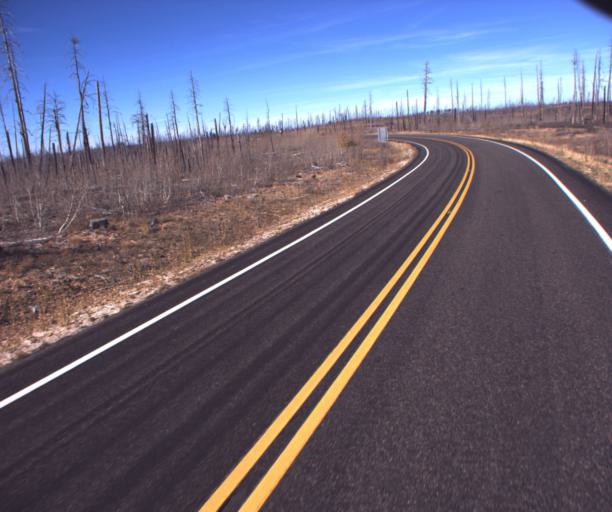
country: US
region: Arizona
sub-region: Coconino County
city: Grand Canyon
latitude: 36.5688
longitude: -112.1730
